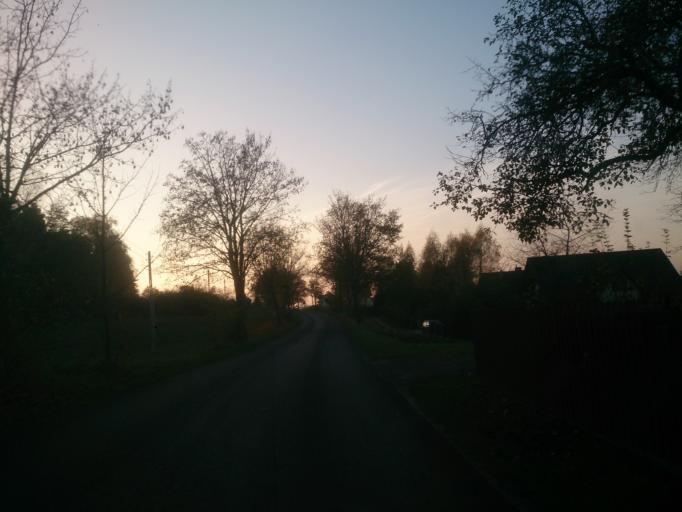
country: PL
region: Kujawsko-Pomorskie
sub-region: Powiat brodnicki
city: Brodnica
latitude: 53.3350
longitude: 19.3915
